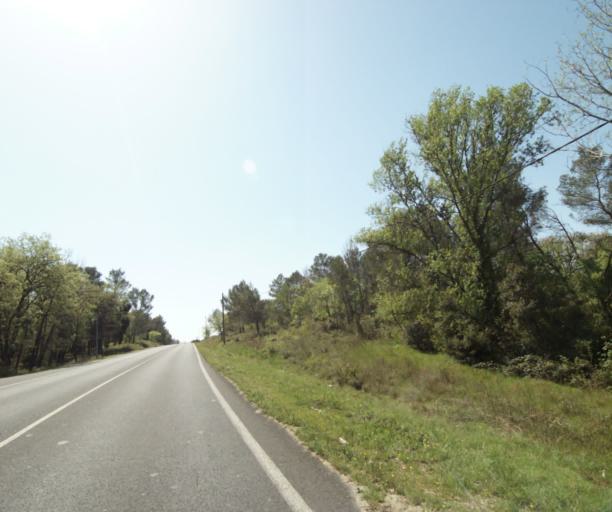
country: FR
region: Languedoc-Roussillon
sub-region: Departement de l'Herault
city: Montferrier-sur-Lez
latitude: 43.6645
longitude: 3.8664
